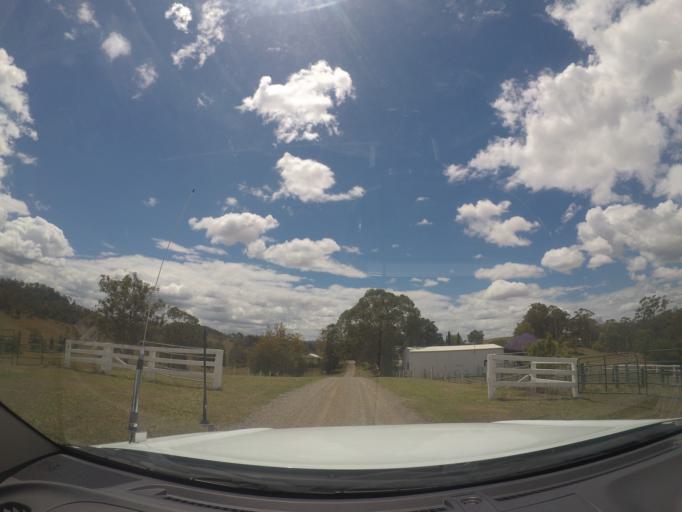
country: AU
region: Queensland
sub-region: Logan
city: Cedar Vale
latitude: -27.9058
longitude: 153.0576
